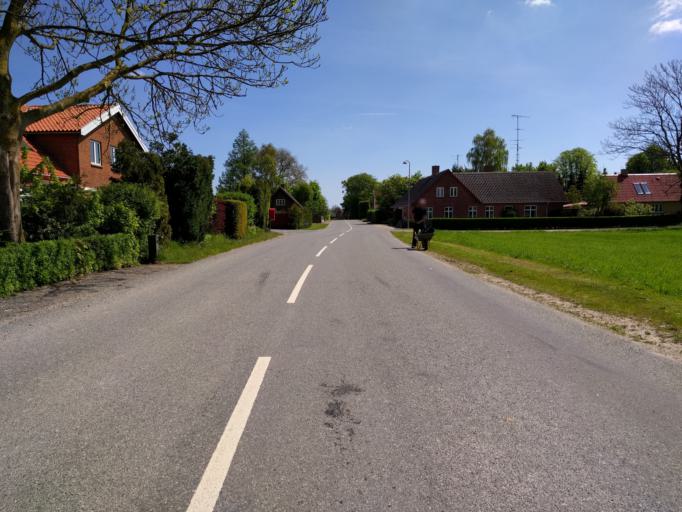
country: DK
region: Zealand
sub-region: Guldborgsund Kommune
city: Nykobing Falster
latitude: 54.7397
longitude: 12.0071
